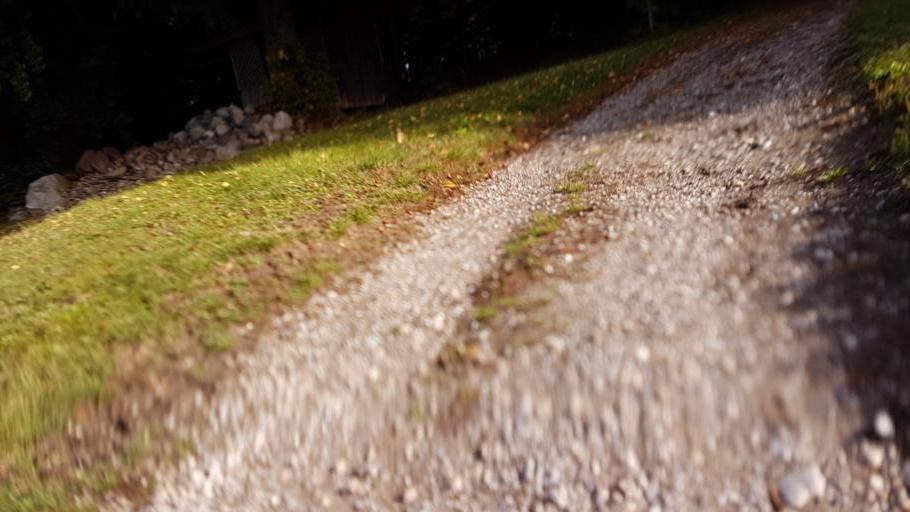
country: CH
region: Bern
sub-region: Bern-Mittelland District
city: Worb
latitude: 46.9229
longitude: 7.5412
